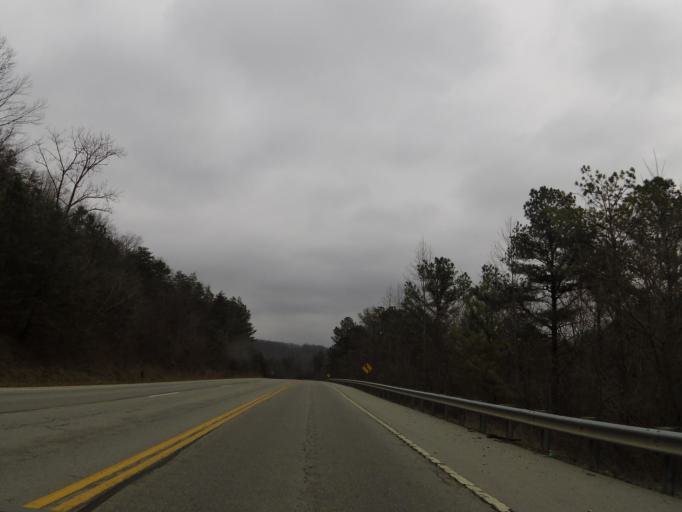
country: US
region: Tennessee
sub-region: Scott County
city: Huntsville
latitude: 36.3759
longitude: -84.5701
